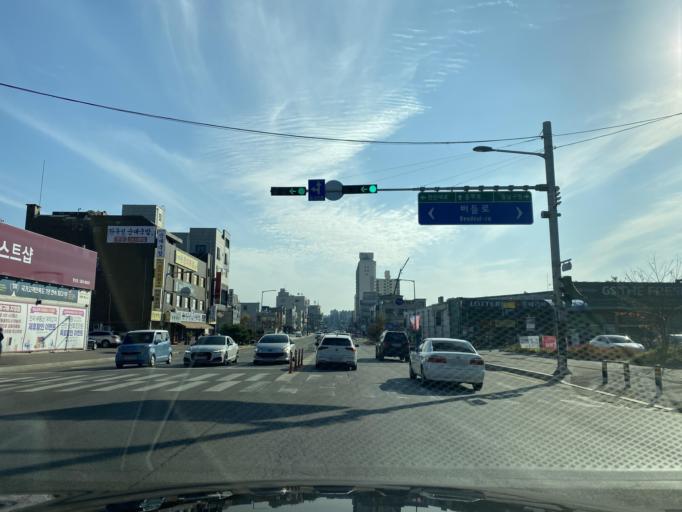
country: KR
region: Chungcheongnam-do
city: Cheonan
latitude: 36.8063
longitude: 127.1587
